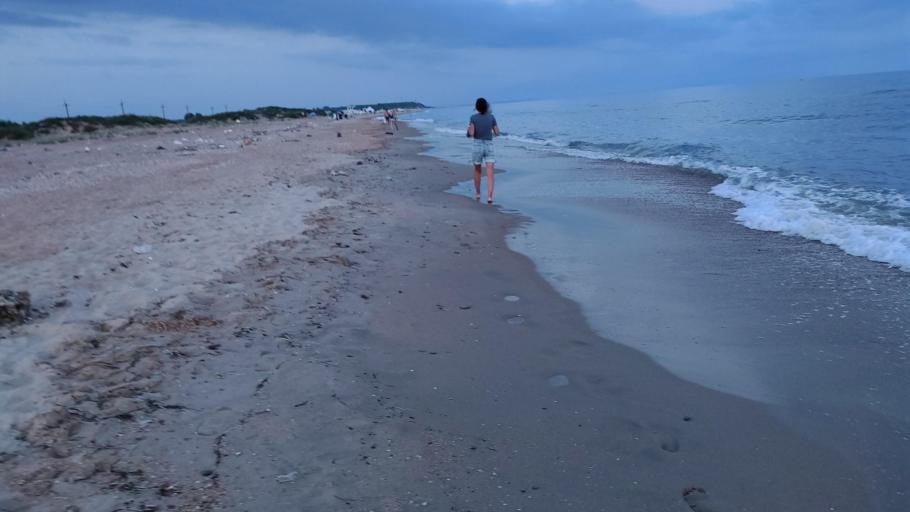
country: RU
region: Krasnodarskiy
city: Blagovetschenskaya
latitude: 45.0677
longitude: 37.0271
